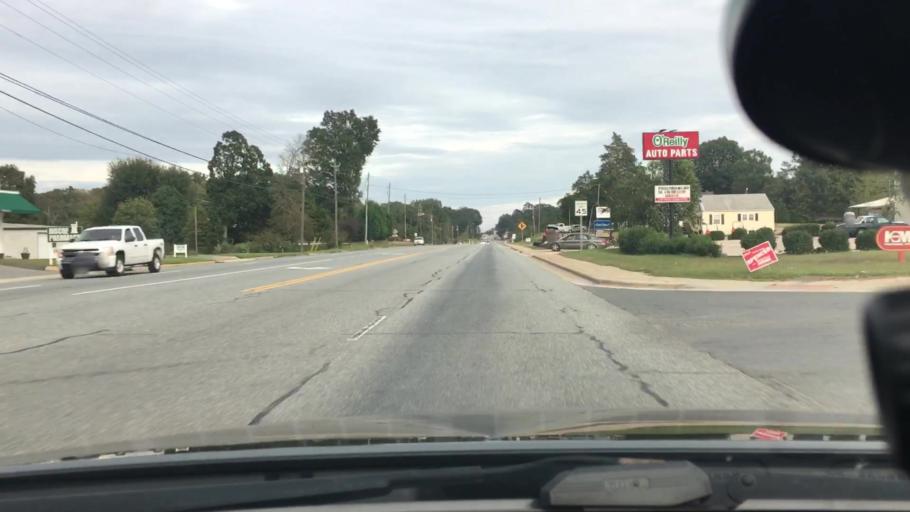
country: US
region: North Carolina
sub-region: Montgomery County
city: Biscoe
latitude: 35.3590
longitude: -79.7950
